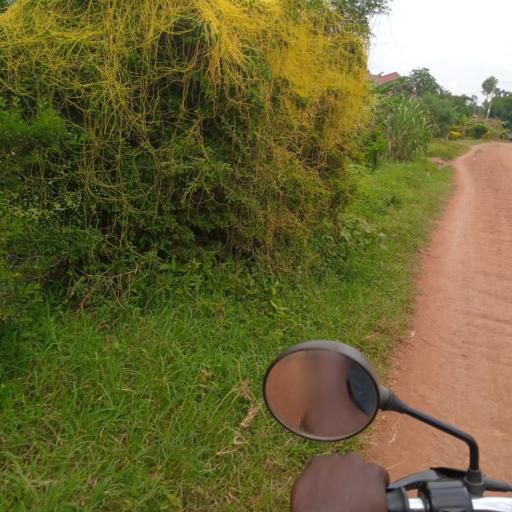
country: UG
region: Eastern Region
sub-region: Mbale District
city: Mbale
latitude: 1.1093
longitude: 34.1818
